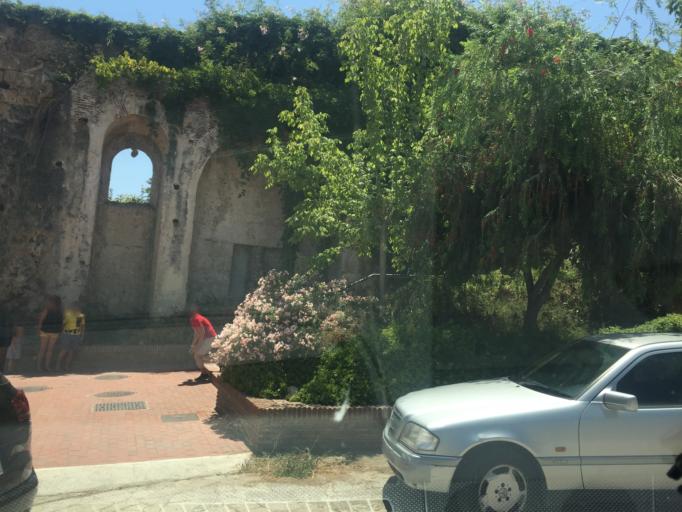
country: ES
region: Andalusia
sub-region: Provincia de Malaga
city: Nerja
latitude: 36.7567
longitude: -3.8423
